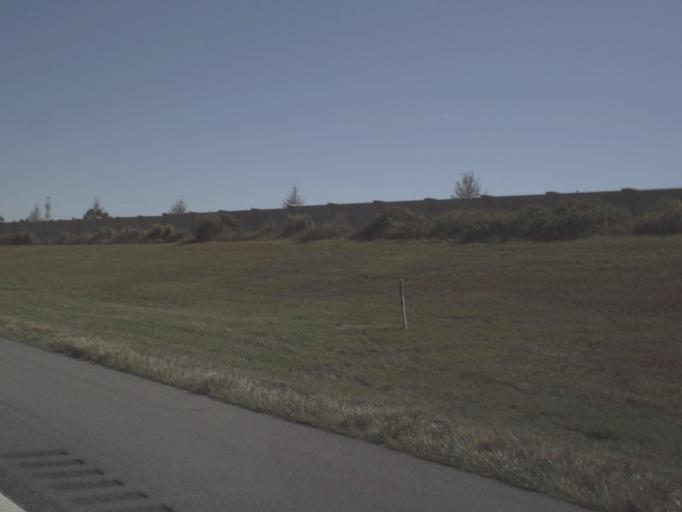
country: US
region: Florida
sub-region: Orange County
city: Oakland
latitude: 28.5532
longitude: -81.6600
